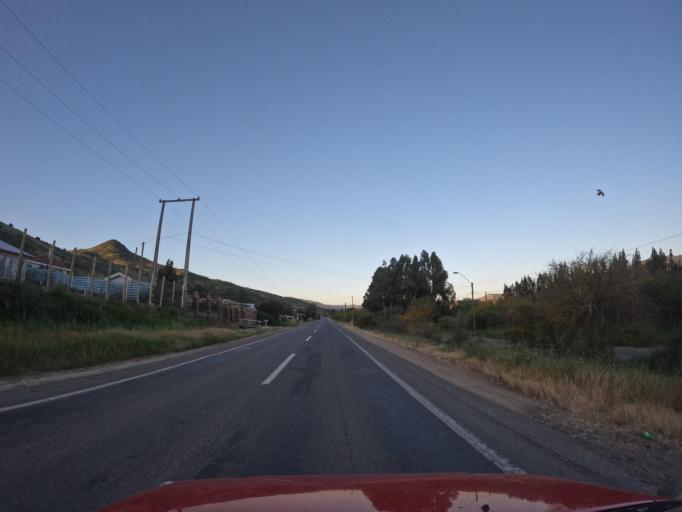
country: CL
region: Maule
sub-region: Provincia de Talca
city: Talca
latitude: -35.0844
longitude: -71.6420
